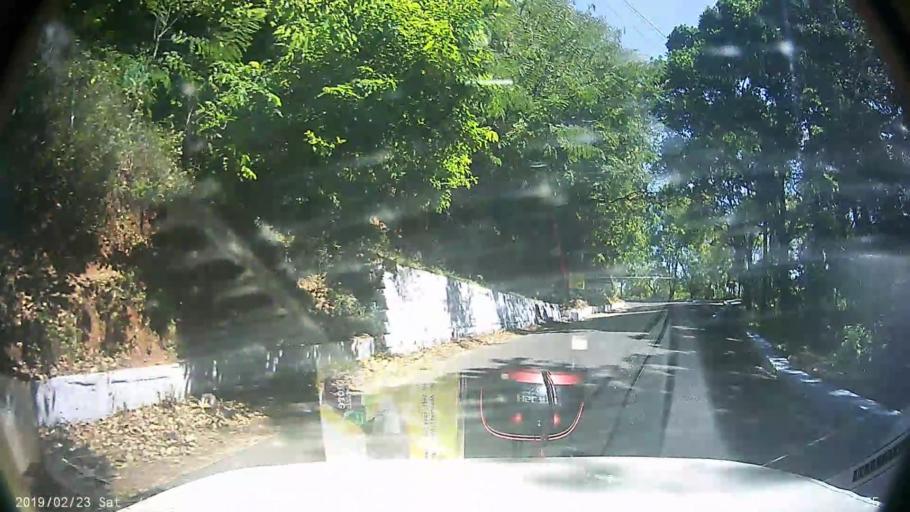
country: IN
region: Tamil Nadu
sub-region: Nilgiri
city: Wellington
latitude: 11.3349
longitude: 76.8264
